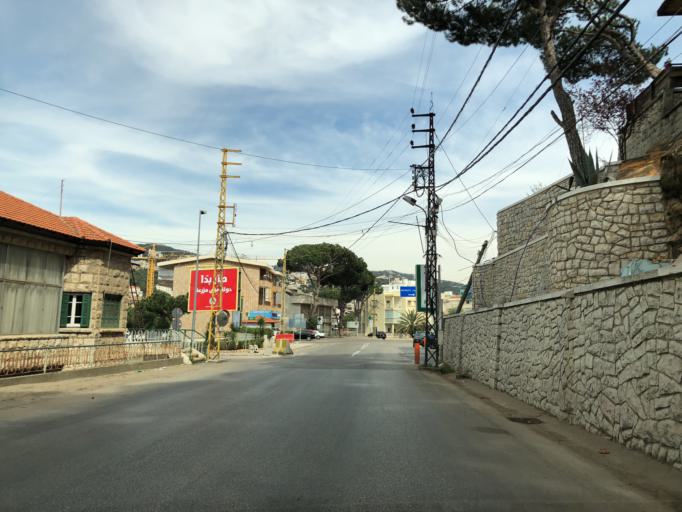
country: LB
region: Mont-Liban
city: Bhamdoun el Mhatta
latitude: 33.8891
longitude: 35.6639
